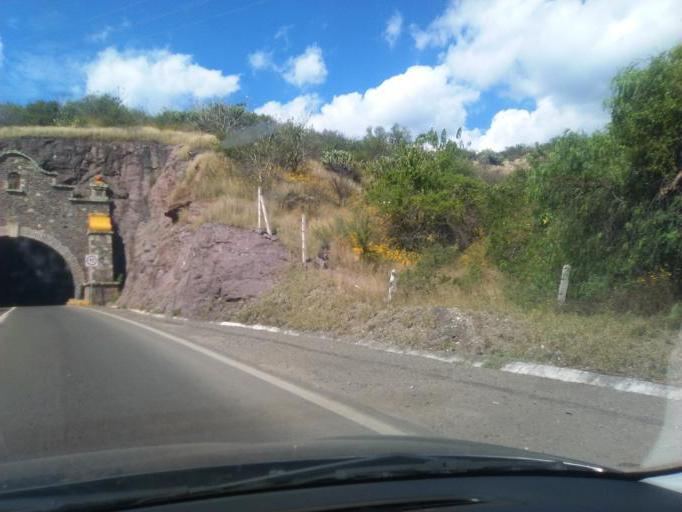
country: MX
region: Guanajuato
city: Marfil
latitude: 21.0023
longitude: -101.2703
